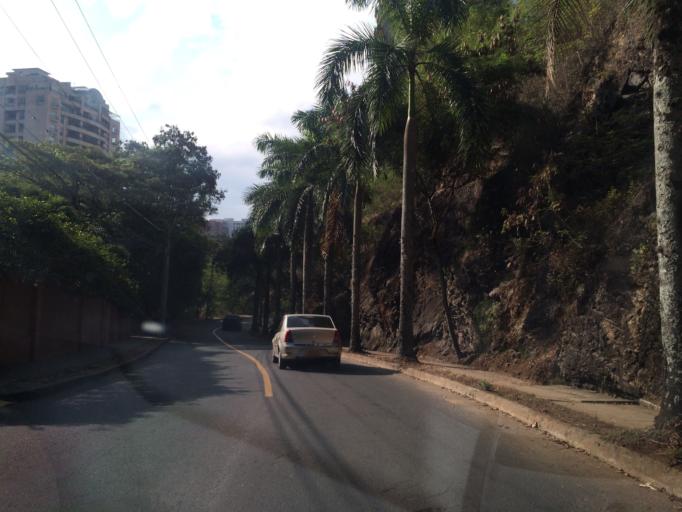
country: CO
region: Valle del Cauca
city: Cali
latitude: 3.4559
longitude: -76.5497
